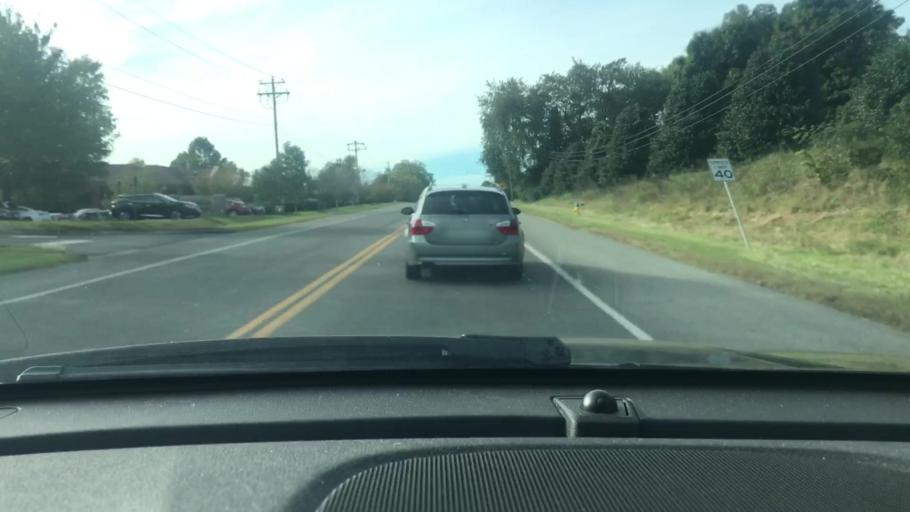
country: US
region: Tennessee
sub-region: Williamson County
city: Franklin
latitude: 35.9249
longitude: -86.8821
